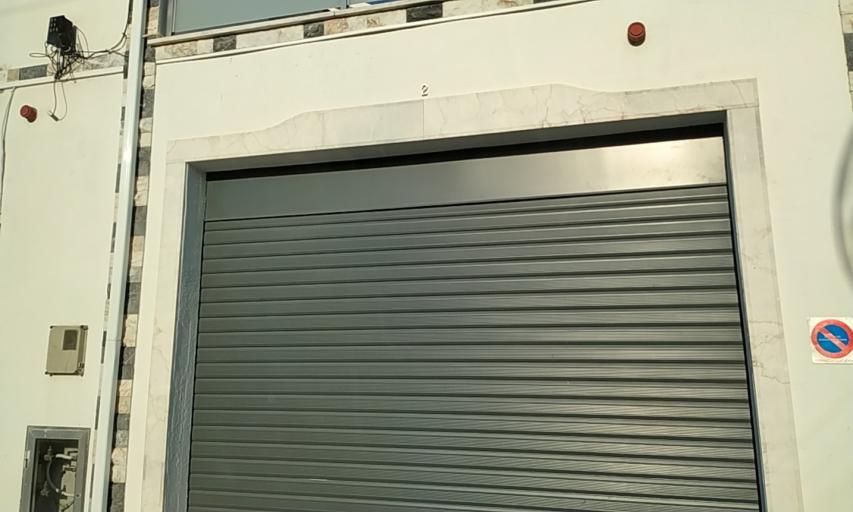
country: PT
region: Santarem
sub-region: Alcanena
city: Alcanena
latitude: 39.3795
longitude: -8.6608
